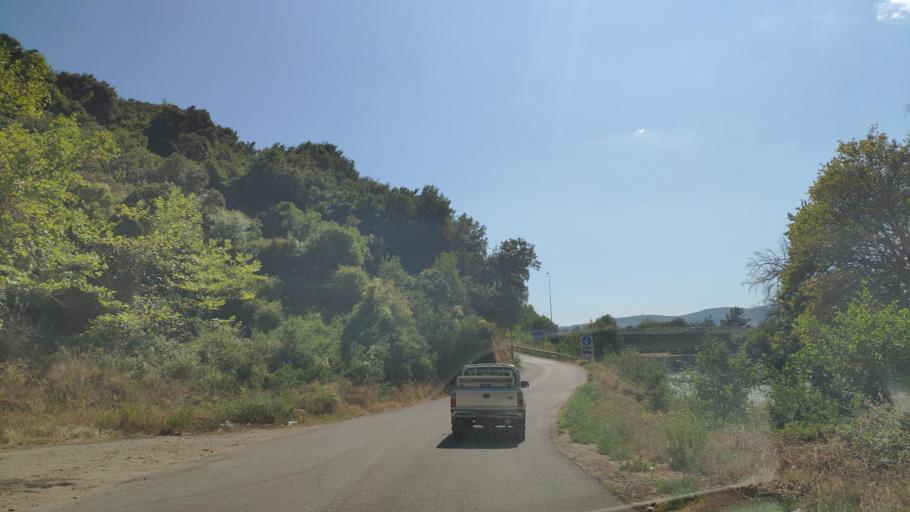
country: GR
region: Epirus
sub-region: Nomos Prevezis
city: Kanalaki
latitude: 39.3229
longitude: 20.6092
